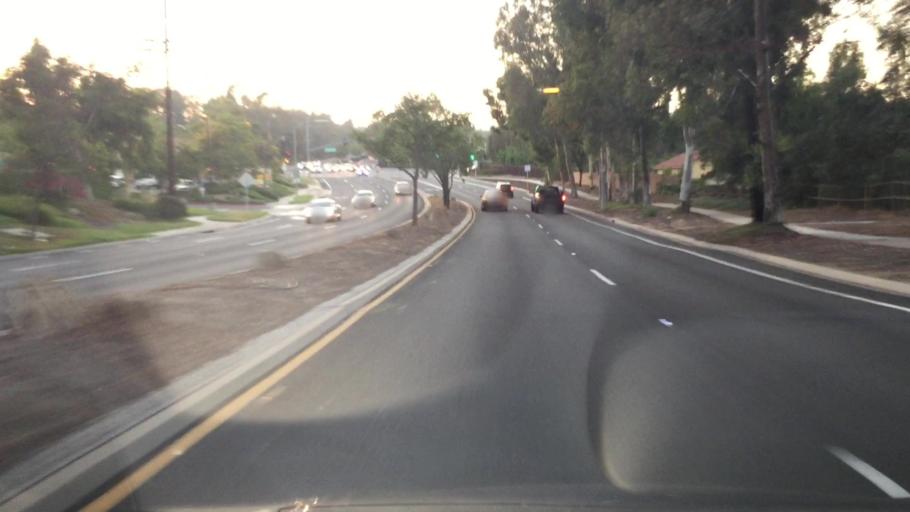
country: US
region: California
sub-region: San Diego County
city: Poway
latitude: 32.9824
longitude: -117.0605
